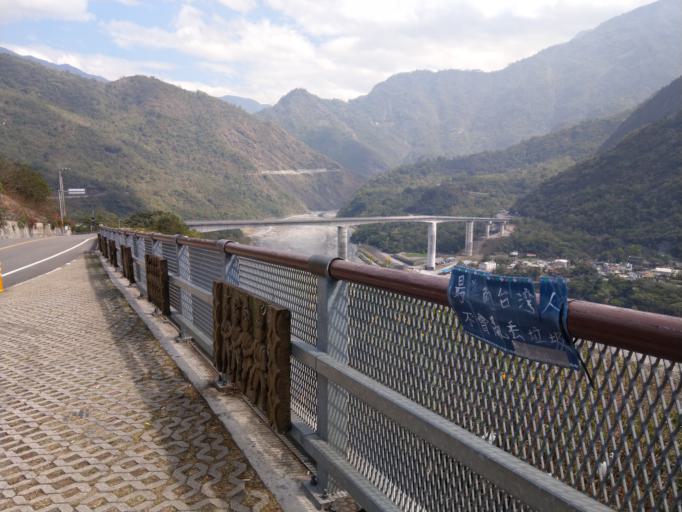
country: TW
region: Taiwan
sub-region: Pingtung
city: Pingtung
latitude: 22.7477
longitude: 120.7006
